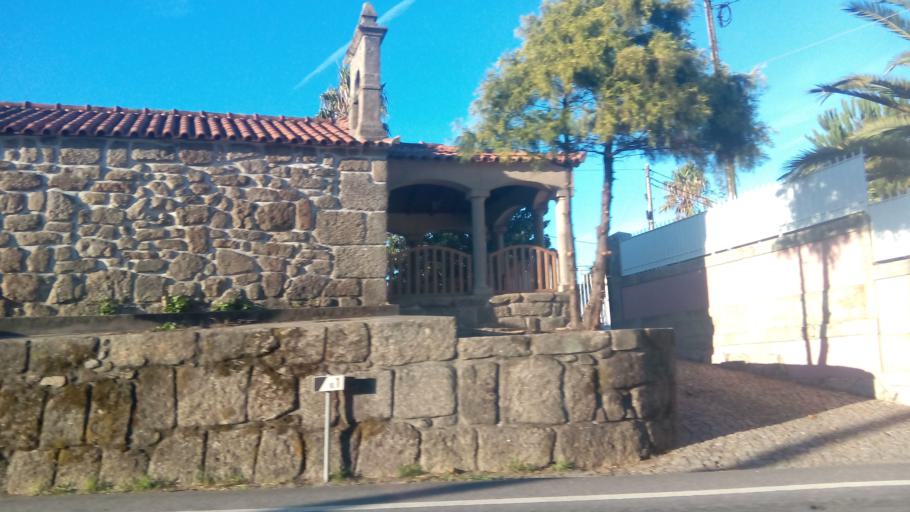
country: PT
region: Porto
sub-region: Paredes
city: Gandra
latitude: 41.1913
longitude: -8.4056
